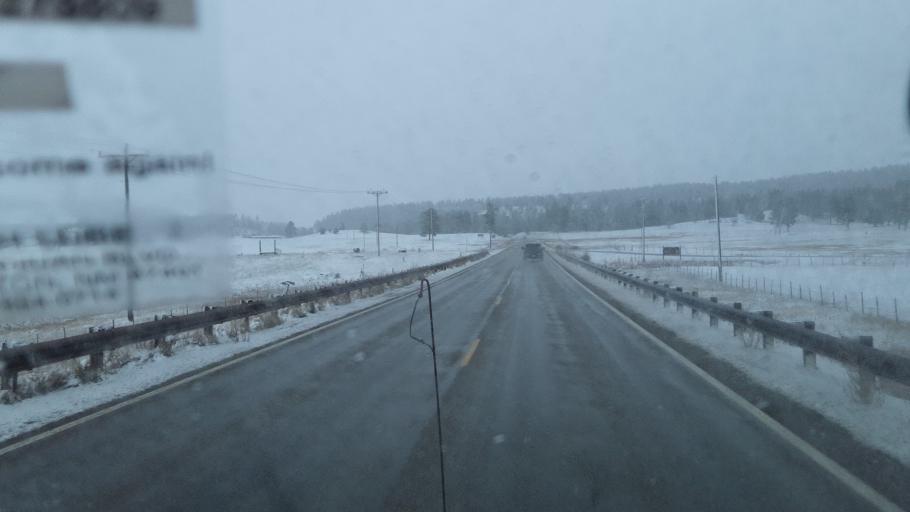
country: US
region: Colorado
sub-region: Archuleta County
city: Pagosa Springs
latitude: 37.1983
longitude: -106.9600
